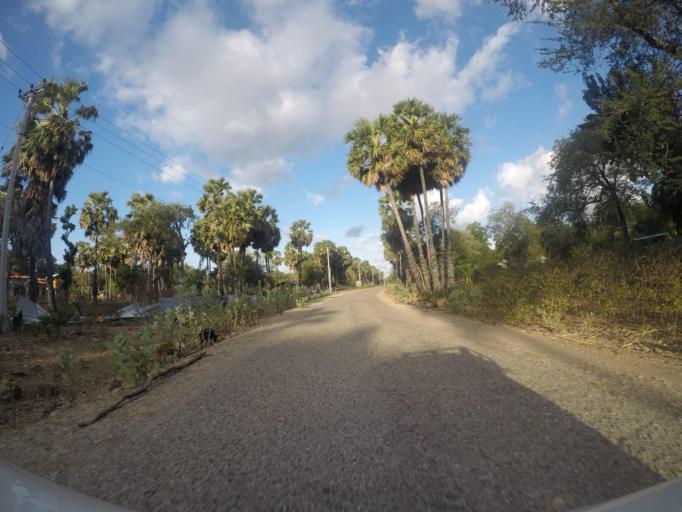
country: TL
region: Lautem
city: Lospalos
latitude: -8.3289
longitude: 126.9656
